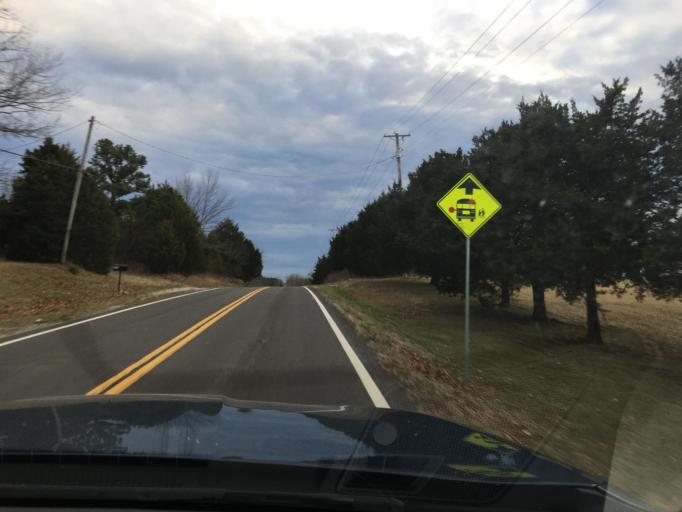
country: US
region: Missouri
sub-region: Jefferson County
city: De Soto
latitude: 38.0986
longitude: -90.5615
